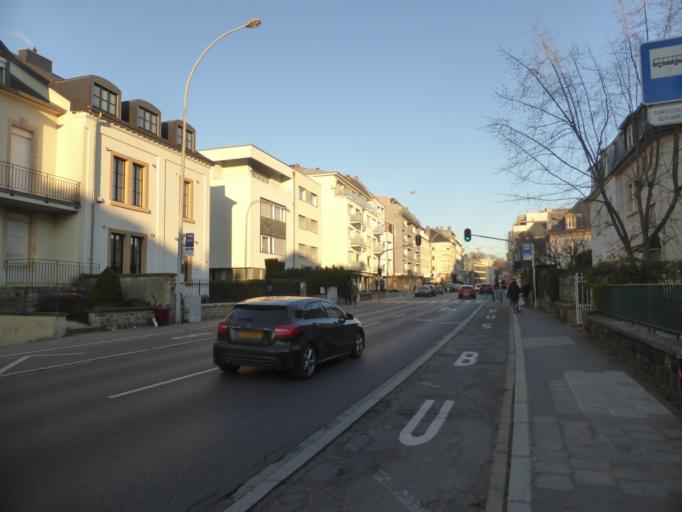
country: LU
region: Luxembourg
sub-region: Canton de Luxembourg
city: Luxembourg
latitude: 49.6085
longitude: 6.1160
